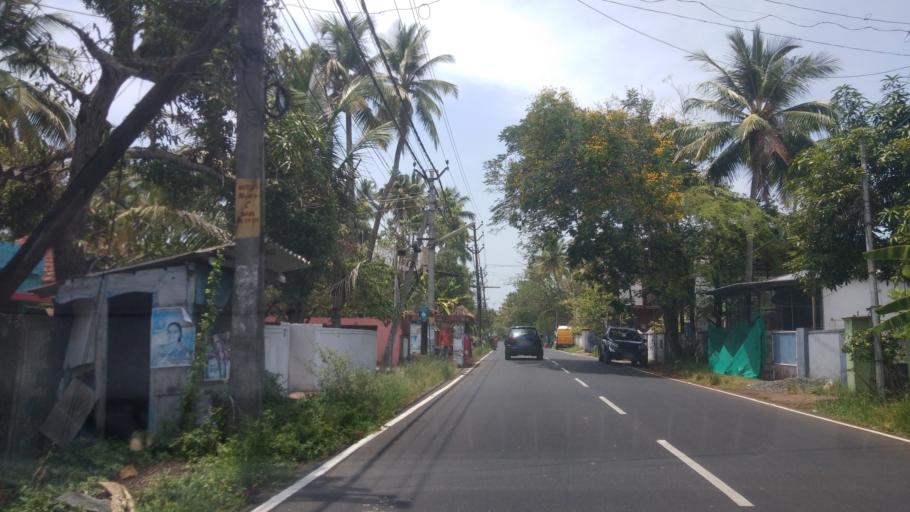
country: IN
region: Kerala
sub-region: Ernakulam
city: Cochin
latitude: 9.8985
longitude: 76.2576
